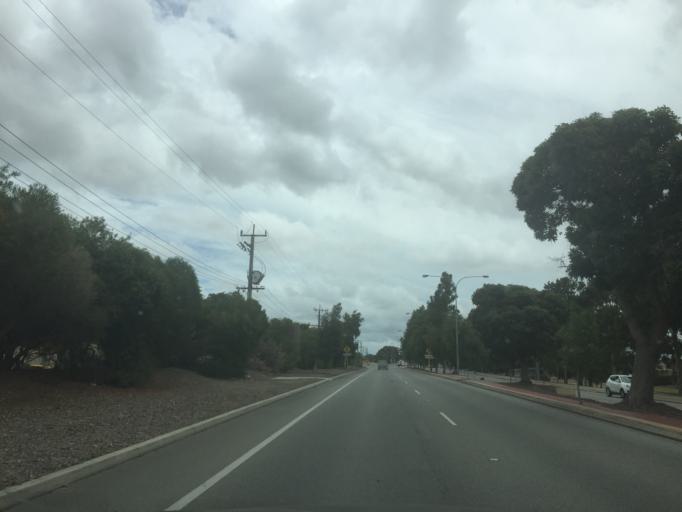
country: AU
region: Western Australia
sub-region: Gosnells
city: Thornlie
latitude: -32.0773
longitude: 115.9459
